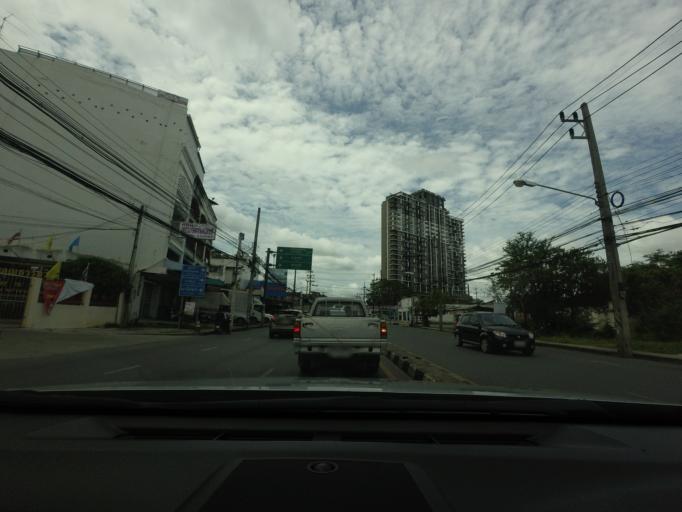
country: TH
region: Songkhla
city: Hat Yai
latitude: 7.0058
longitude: 100.4608
